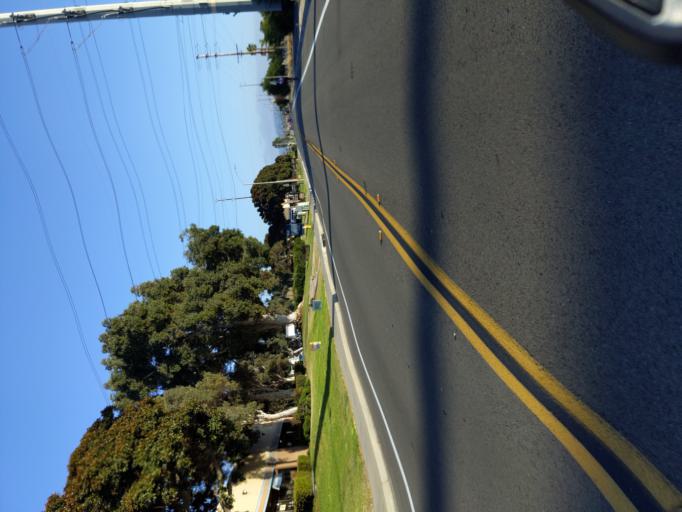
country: US
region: California
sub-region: San Diego County
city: Imperial Beach
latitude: 32.6083
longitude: -117.0922
